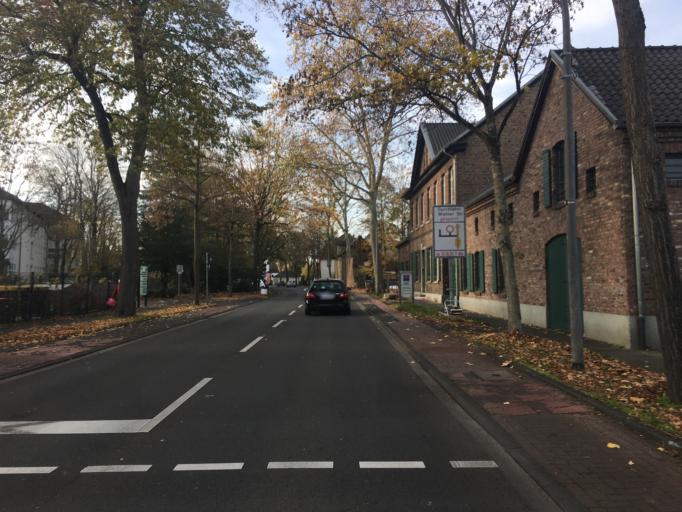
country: DE
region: North Rhine-Westphalia
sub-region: Regierungsbezirk Koln
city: Merheim
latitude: 50.9463
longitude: 7.0719
